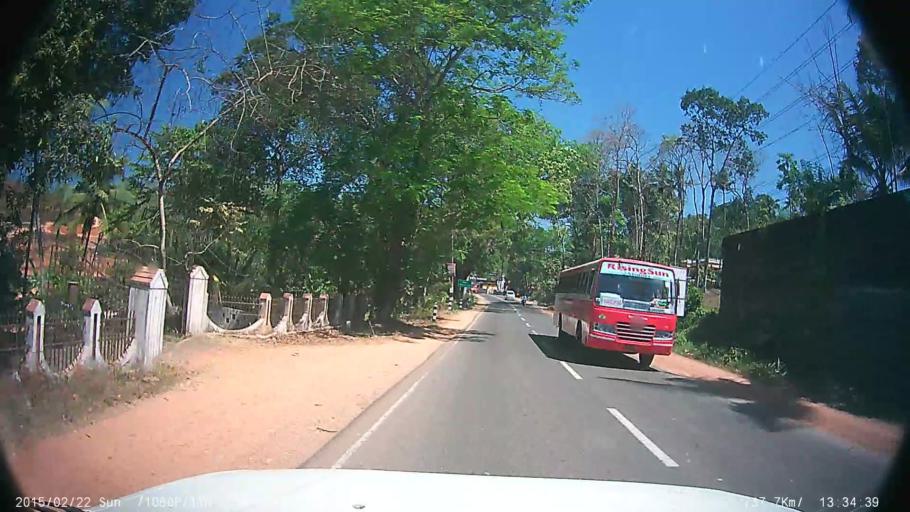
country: IN
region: Kerala
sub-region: Kottayam
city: Changanacheri
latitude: 9.4799
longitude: 76.6018
